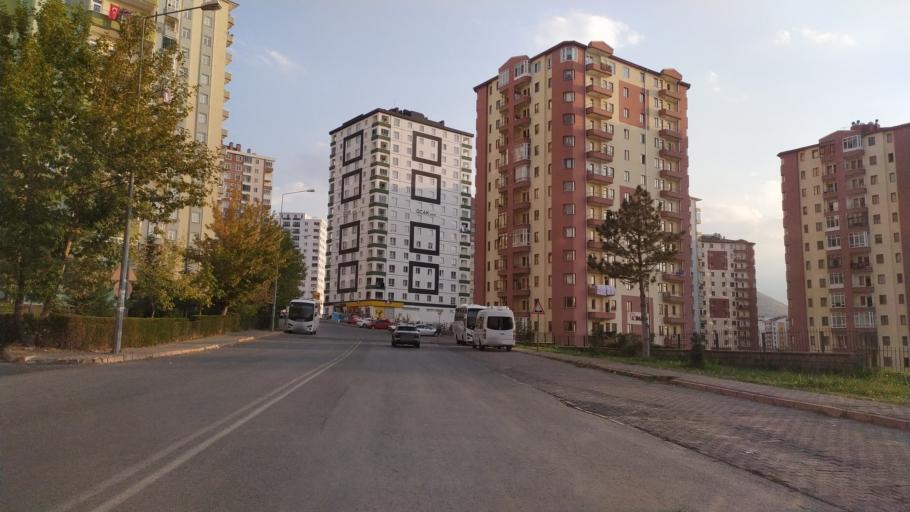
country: TR
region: Kayseri
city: Talas
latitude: 38.7045
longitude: 35.5615
